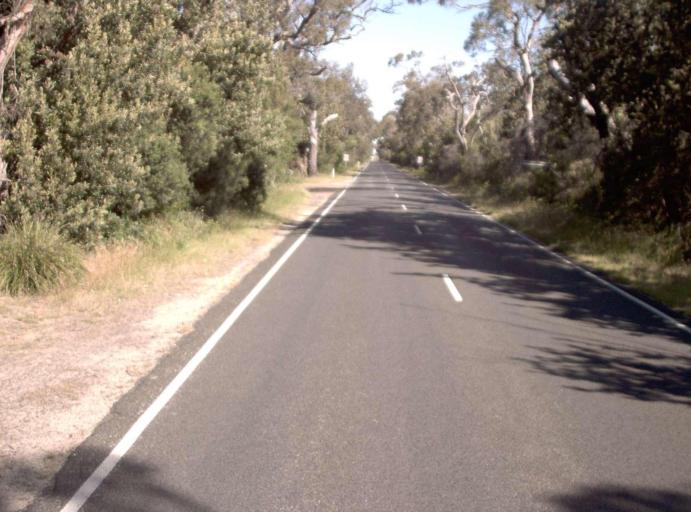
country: AU
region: Victoria
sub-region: Latrobe
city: Traralgon
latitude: -38.6577
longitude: 146.6806
